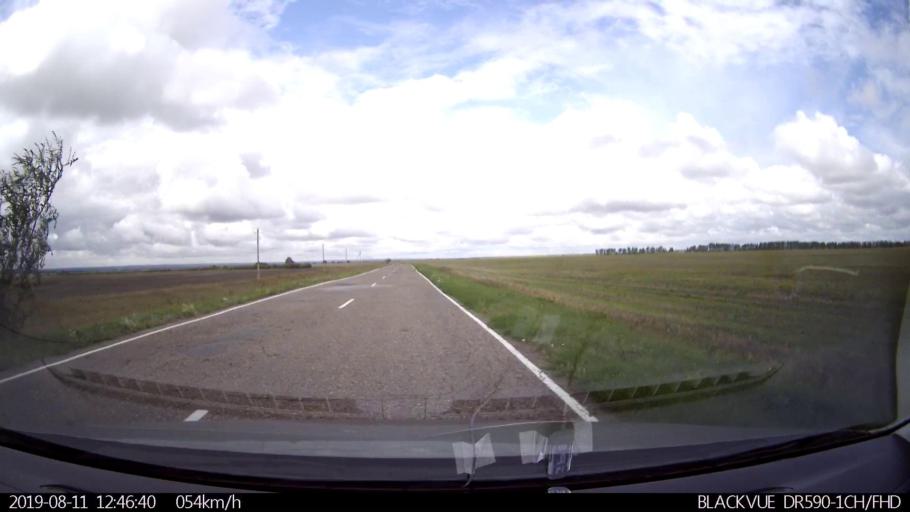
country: RU
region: Ulyanovsk
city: Ignatovka
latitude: 53.8655
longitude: 47.7165
